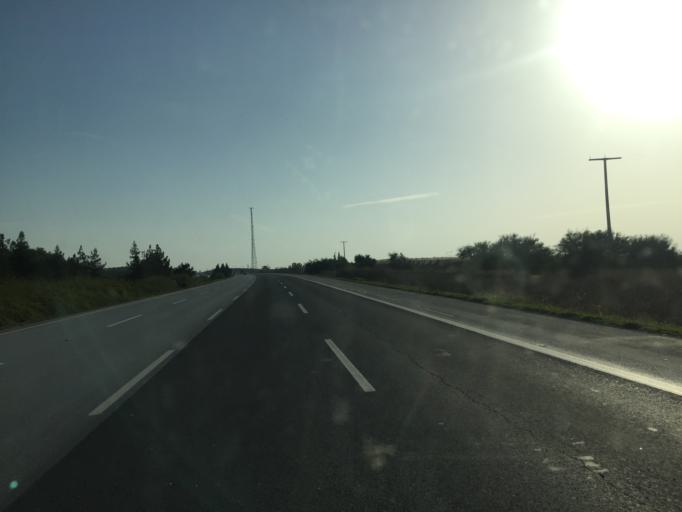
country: TR
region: Mersin
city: Yenice
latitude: 37.0229
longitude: 35.0779
